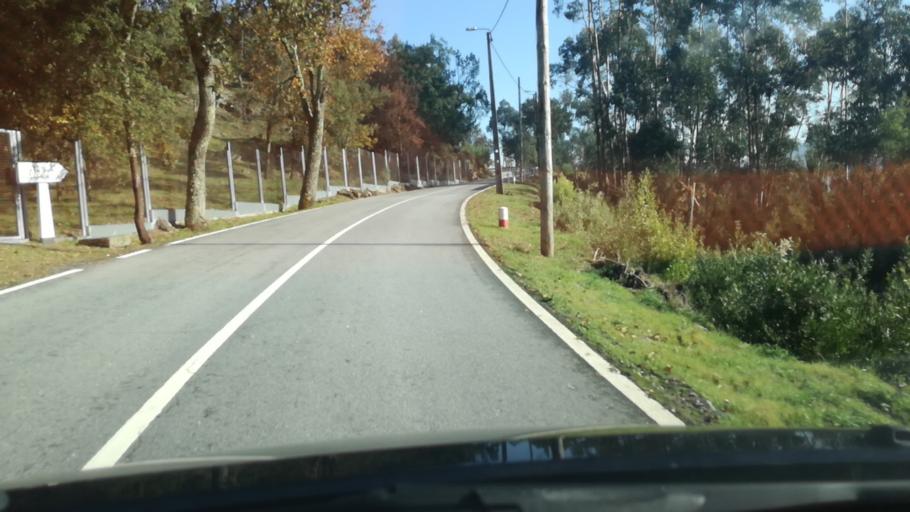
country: PT
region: Braga
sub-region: Guimaraes
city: Ponte
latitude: 41.5259
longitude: -8.3167
